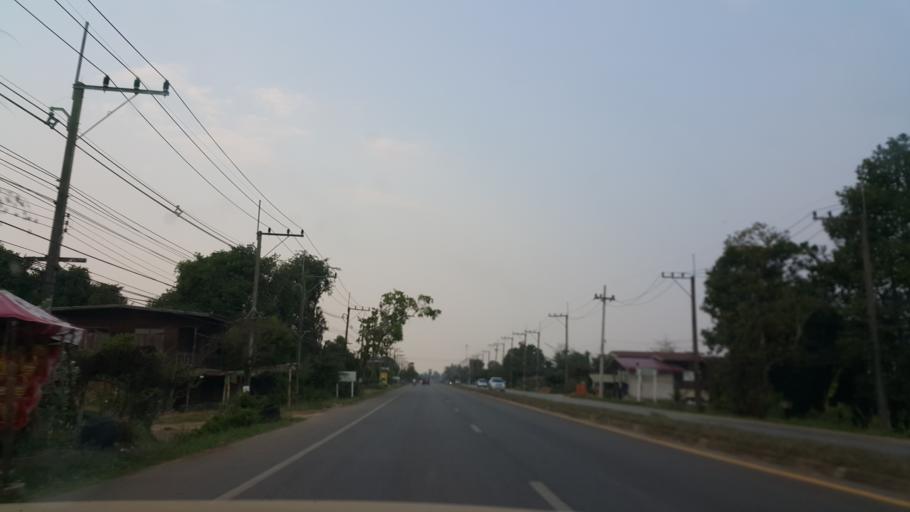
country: TH
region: Nakhon Phanom
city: That Phanom
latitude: 17.0002
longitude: 104.7233
